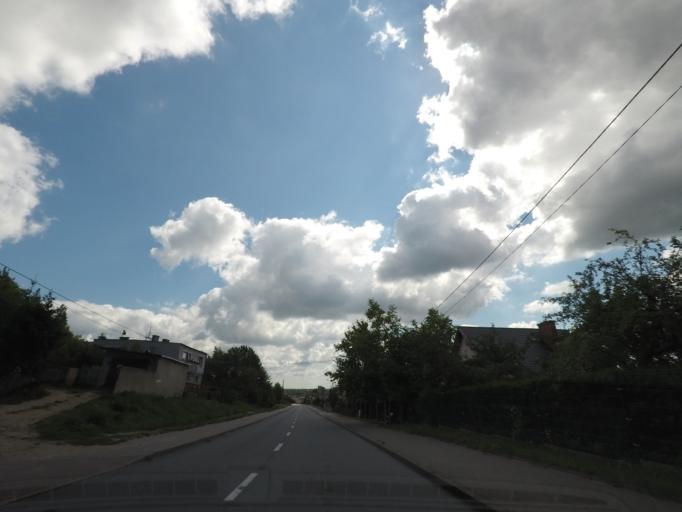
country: PL
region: Pomeranian Voivodeship
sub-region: Powiat wejherowski
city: Leczyce
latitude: 54.5948
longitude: 17.8544
